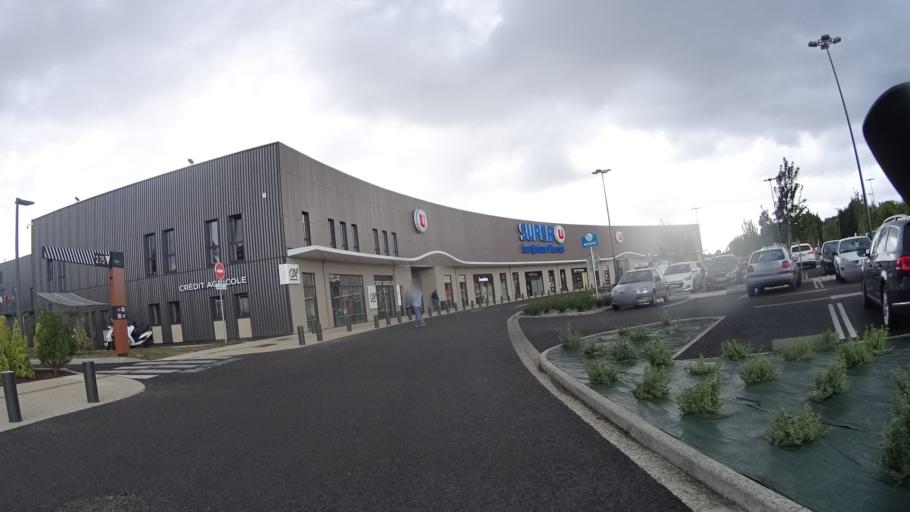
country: FR
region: Centre
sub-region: Departement du Loiret
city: Saint-Pryve-Saint-Mesmin
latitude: 47.8818
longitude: 1.8639
